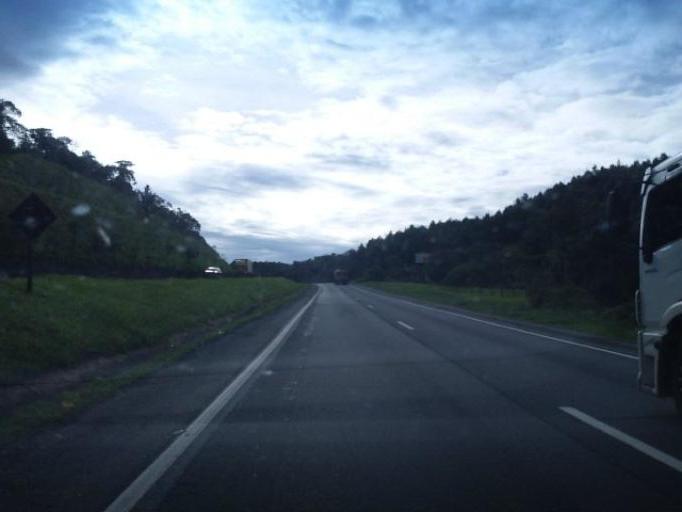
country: BR
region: Parana
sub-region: Antonina
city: Antonina
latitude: -25.0998
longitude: -48.6927
